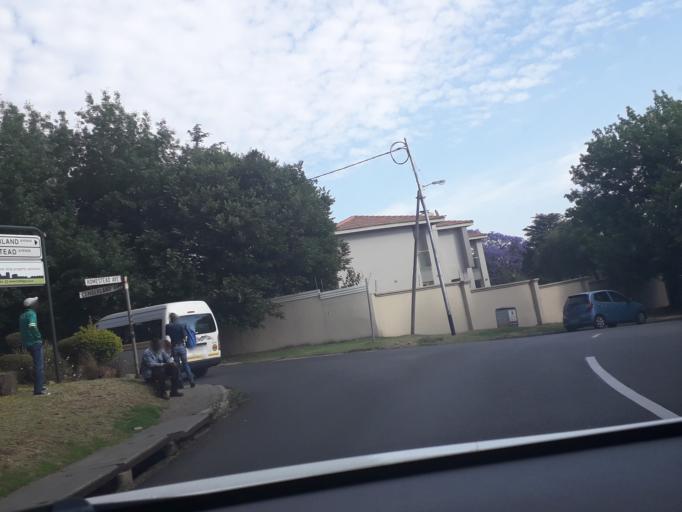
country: ZA
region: Gauteng
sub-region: City of Johannesburg Metropolitan Municipality
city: Diepsloot
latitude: -26.0659
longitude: 28.0003
